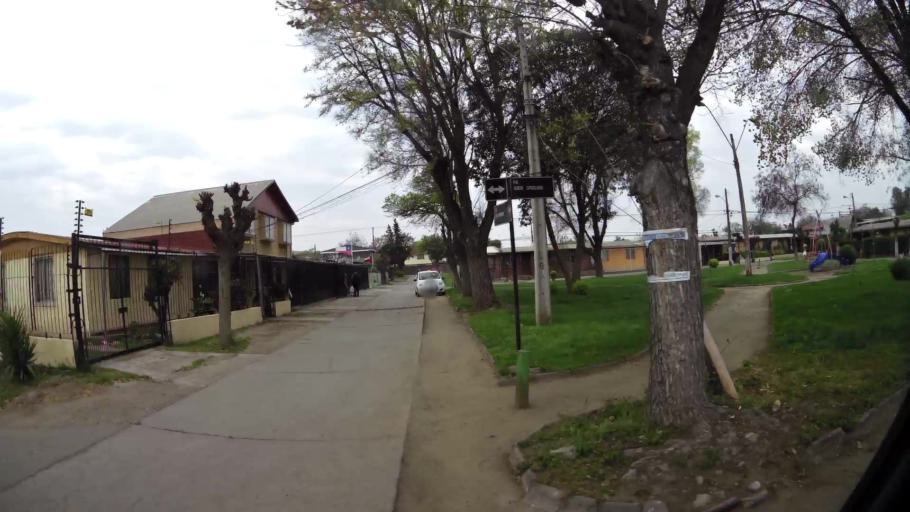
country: CL
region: Santiago Metropolitan
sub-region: Provincia de Santiago
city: Lo Prado
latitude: -33.5042
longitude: -70.7471
